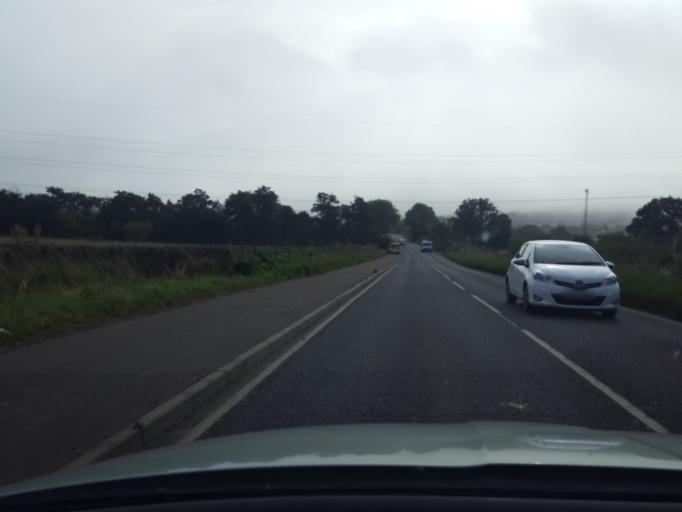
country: GB
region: Scotland
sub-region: Fife
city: Inverkeithing
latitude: 56.0432
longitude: -3.3923
